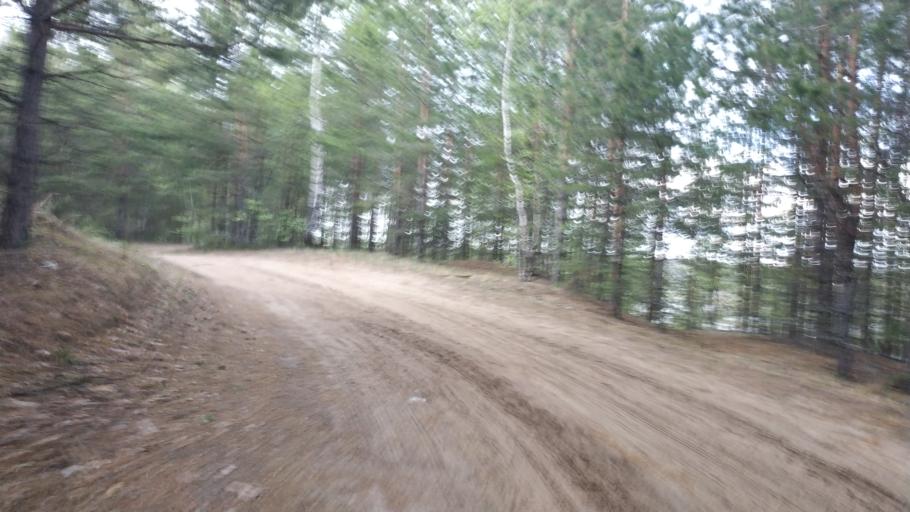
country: RU
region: Chuvashia
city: Novocheboksarsk
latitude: 56.1619
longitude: 47.4627
